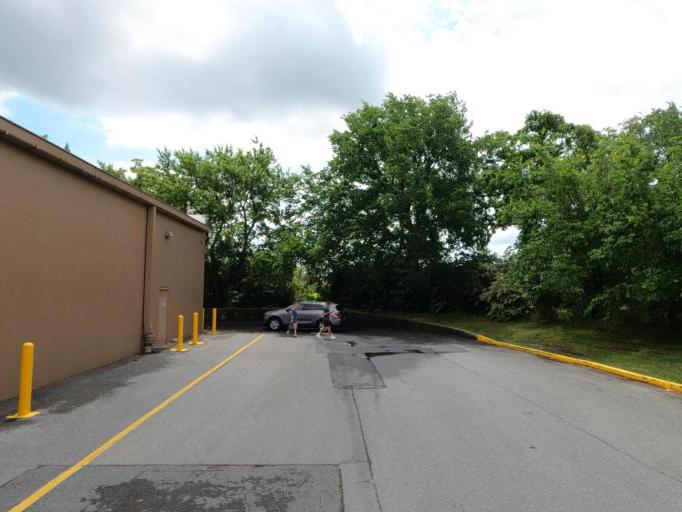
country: US
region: Delaware
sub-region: Sussex County
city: Lewes
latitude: 38.7268
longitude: -75.1326
